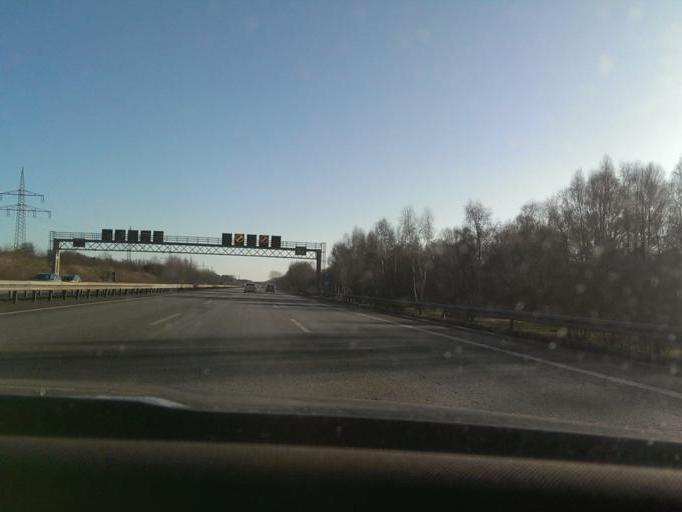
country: DE
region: Lower Saxony
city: Langenhagen
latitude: 52.4274
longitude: 9.7454
